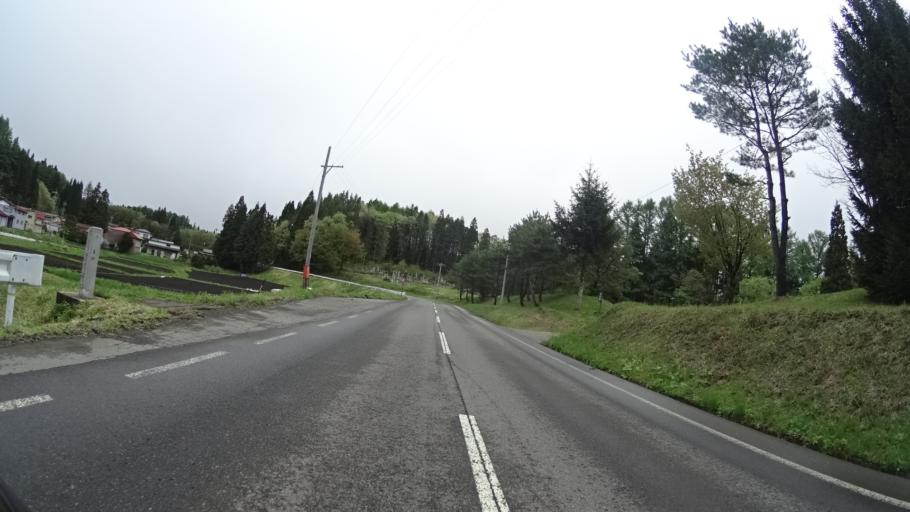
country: JP
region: Nagano
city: Nagano-shi
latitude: 36.7586
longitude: 138.1985
